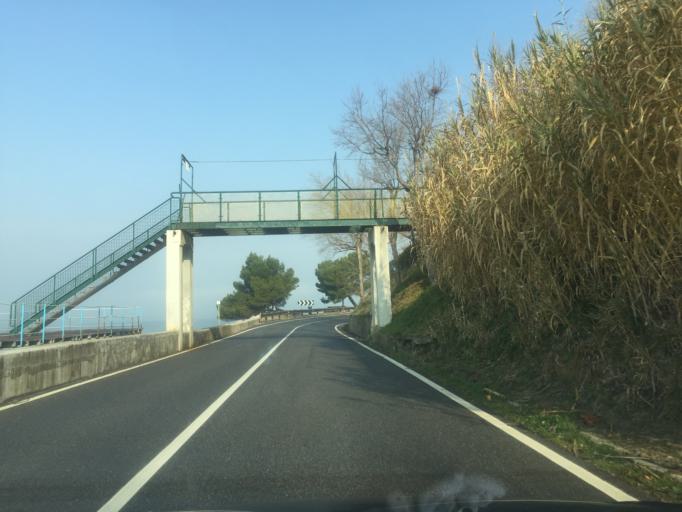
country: SI
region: Koper-Capodistria
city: Ankaran
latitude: 45.6049
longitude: 13.7193
